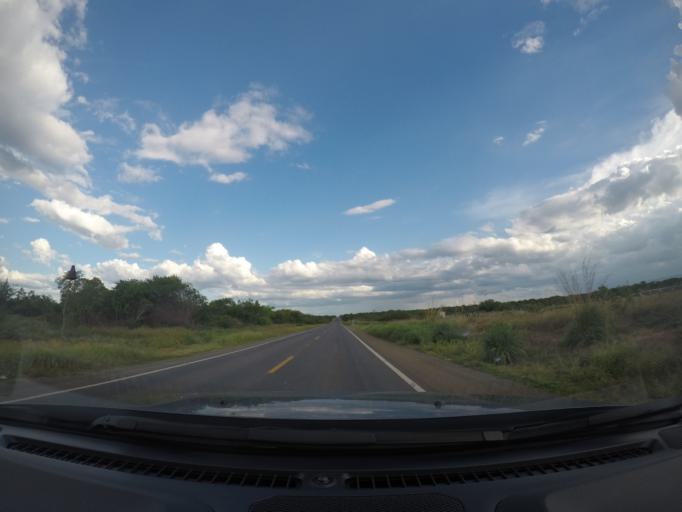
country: BR
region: Bahia
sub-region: Oliveira Dos Brejinhos
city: Beira Rio
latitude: -12.1952
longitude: -42.8189
